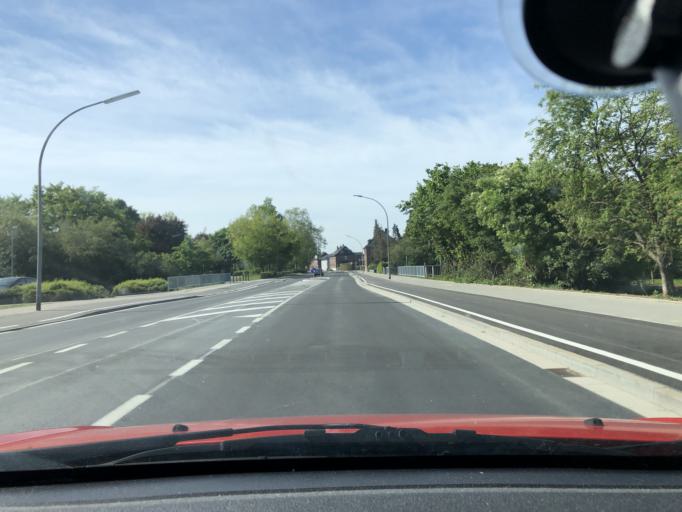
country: DE
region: North Rhine-Westphalia
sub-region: Regierungsbezirk Dusseldorf
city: Kamp-Lintfort
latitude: 51.5016
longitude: 6.5357
